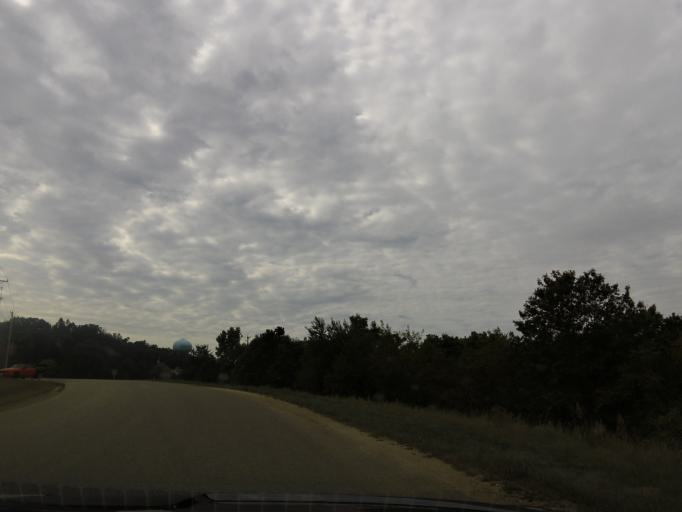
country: US
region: Wisconsin
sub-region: Monroe County
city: Sparta
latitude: 43.9437
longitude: -90.7702
